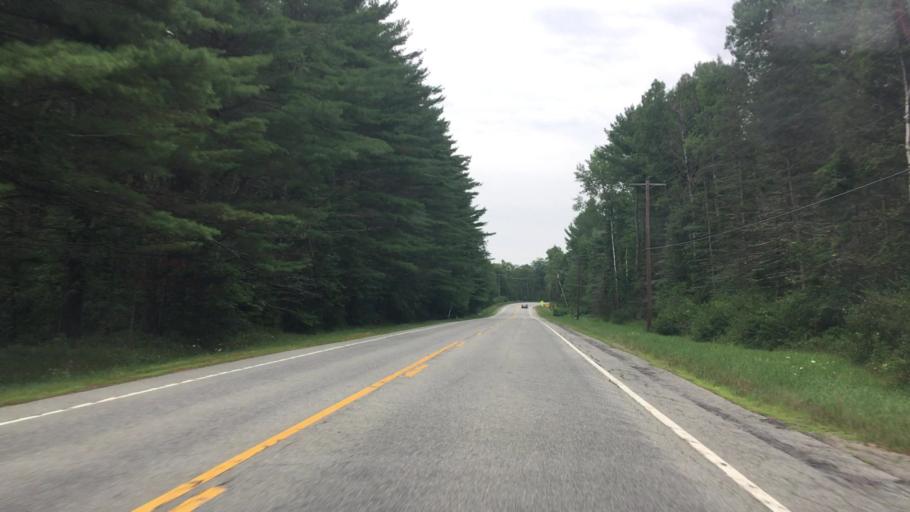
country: US
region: New York
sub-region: Essex County
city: Lake Placid
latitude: 44.2705
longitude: -73.7909
